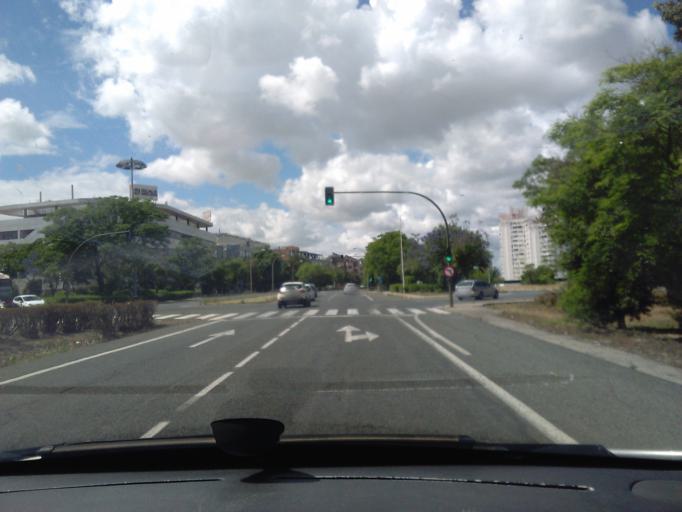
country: ES
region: Andalusia
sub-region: Provincia de Sevilla
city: Sevilla
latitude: 37.3458
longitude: -5.9751
